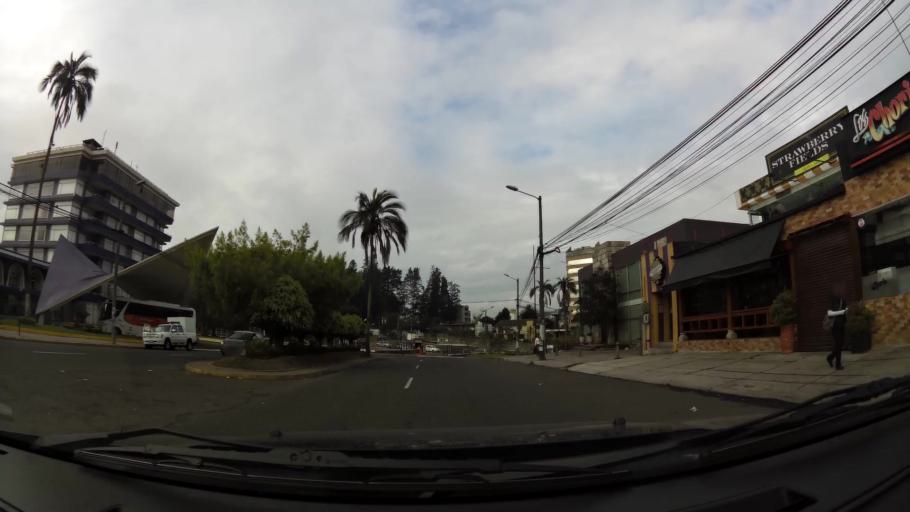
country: EC
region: Pichincha
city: Quito
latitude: -0.2016
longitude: -78.4803
